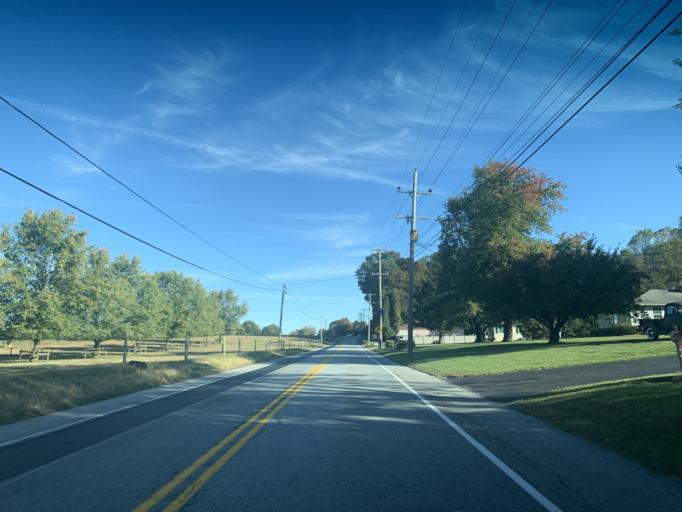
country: US
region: Pennsylvania
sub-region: Chester County
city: Parkesburg
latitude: 39.8683
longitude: -75.9238
